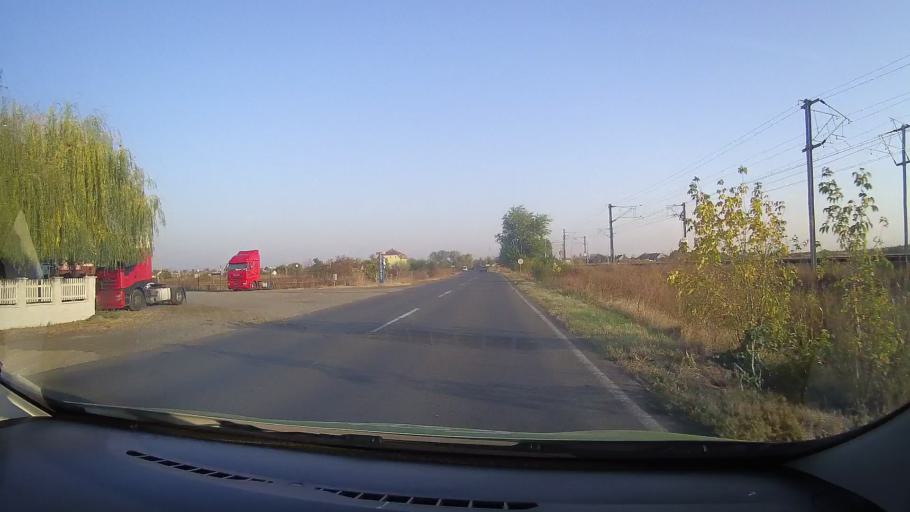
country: RO
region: Arad
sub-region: Comuna Sofronea
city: Sofronea
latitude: 46.2710
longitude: 21.3155
